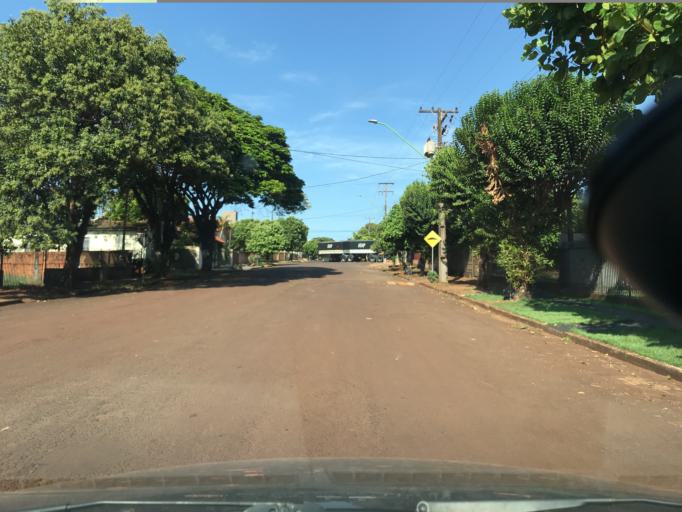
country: BR
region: Parana
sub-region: Palotina
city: Palotina
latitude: -24.2883
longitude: -53.8337
